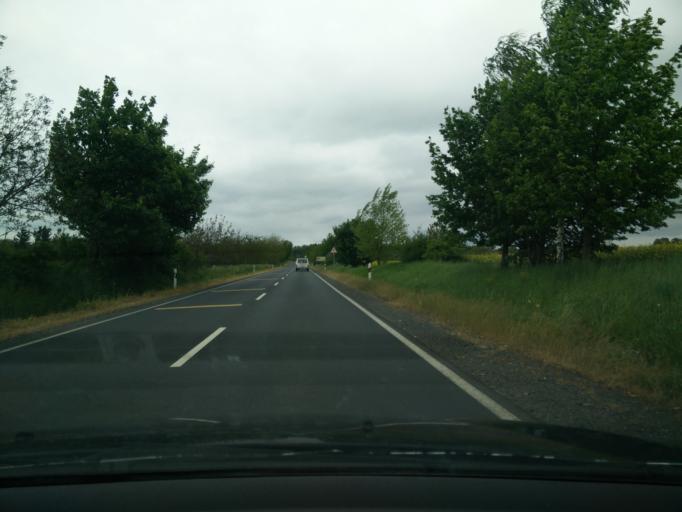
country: HU
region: Zala
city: Turje
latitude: 46.9818
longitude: 17.1167
